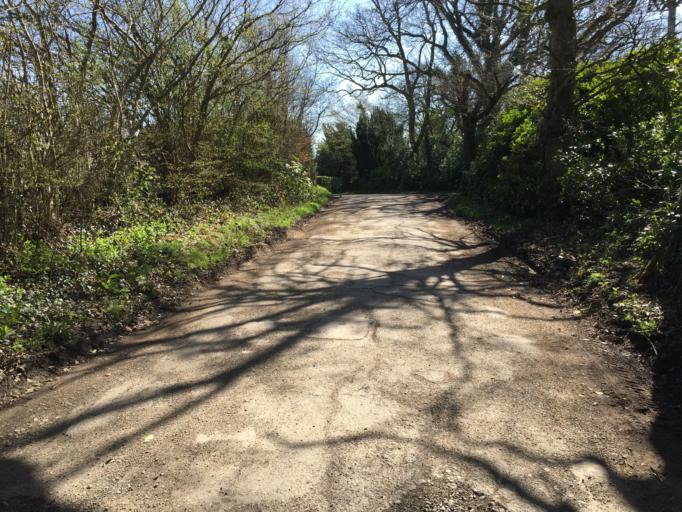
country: GB
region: England
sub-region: East Sussex
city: Wadhurst
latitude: 51.0325
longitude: 0.2852
